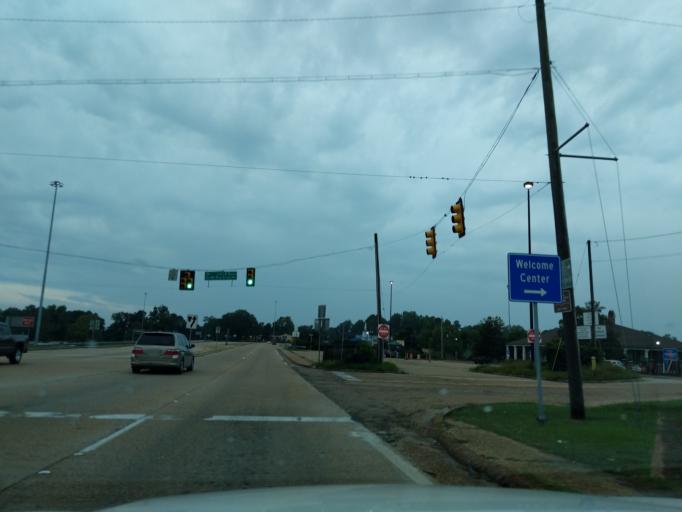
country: US
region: Mississippi
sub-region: Warren County
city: Vicksburg
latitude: 32.3124
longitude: -90.8997
